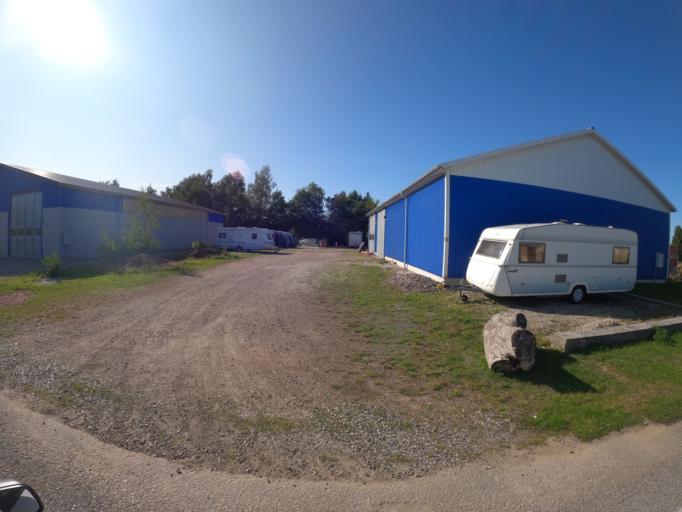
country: SE
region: Skane
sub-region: Lunds Kommun
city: Genarp
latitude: 55.7182
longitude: 13.3652
